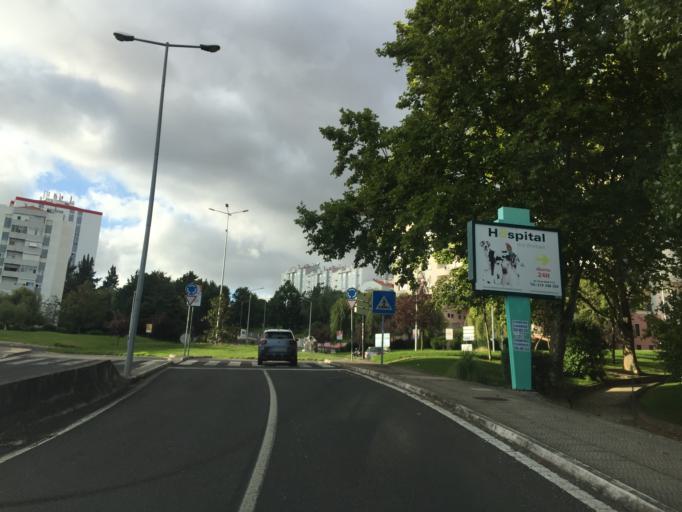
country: PT
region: Lisbon
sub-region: Odivelas
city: Ramada
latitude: 38.8037
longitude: -9.1862
